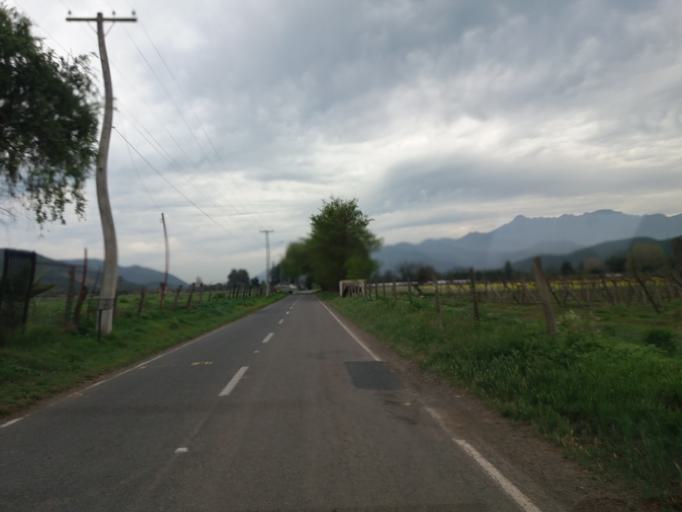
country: CL
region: Valparaiso
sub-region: Provincia de Quillota
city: Quillota
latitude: -32.8909
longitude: -71.1078
